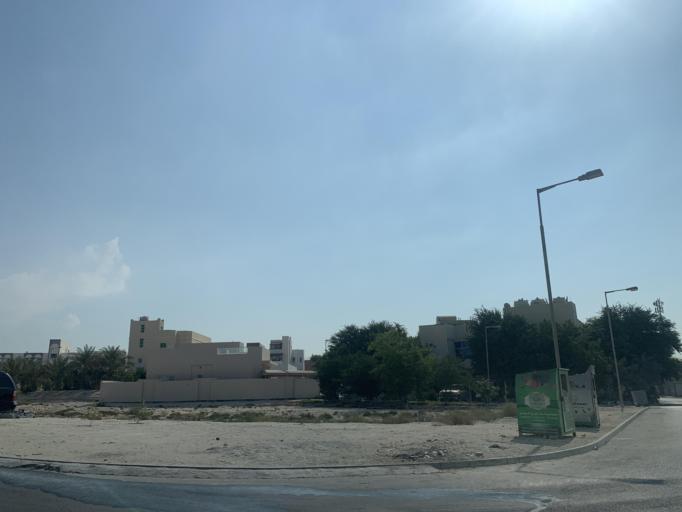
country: BH
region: Central Governorate
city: Madinat Hamad
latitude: 26.1001
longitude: 50.5004
